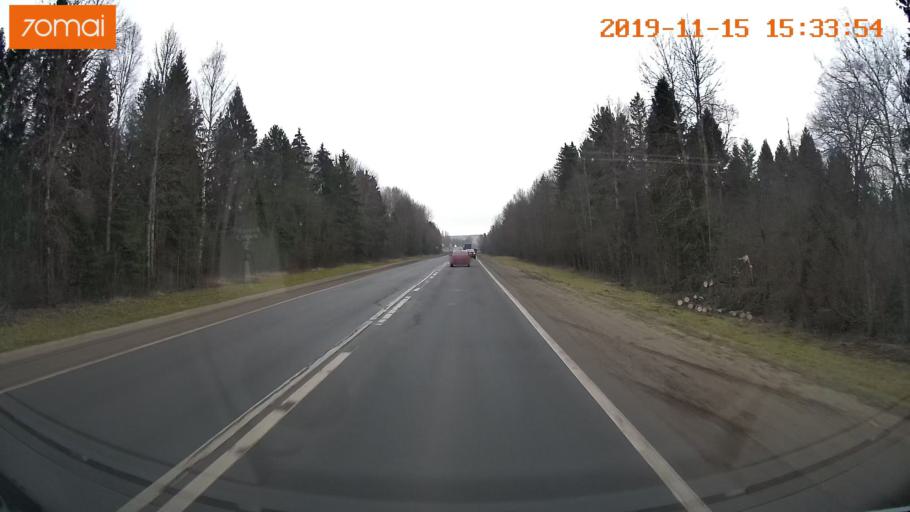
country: RU
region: Jaroslavl
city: Danilov
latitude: 58.0752
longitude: 40.0909
